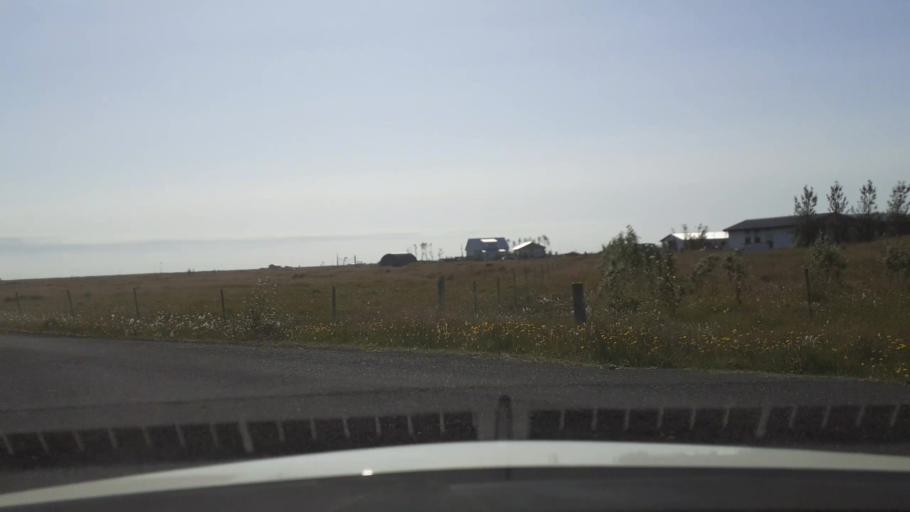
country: IS
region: South
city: Selfoss
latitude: 63.8972
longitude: -21.0828
